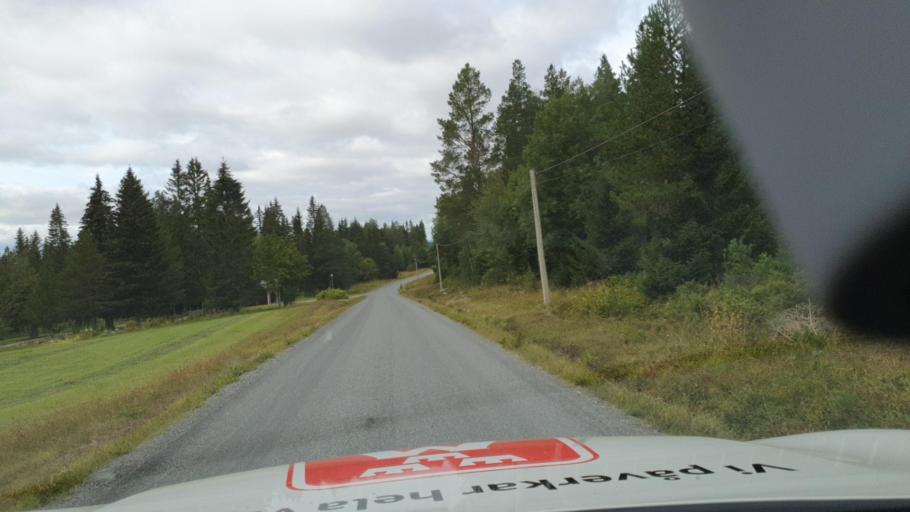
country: SE
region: Jaemtland
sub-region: OEstersunds Kommun
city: Ostersund
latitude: 63.1407
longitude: 14.5607
